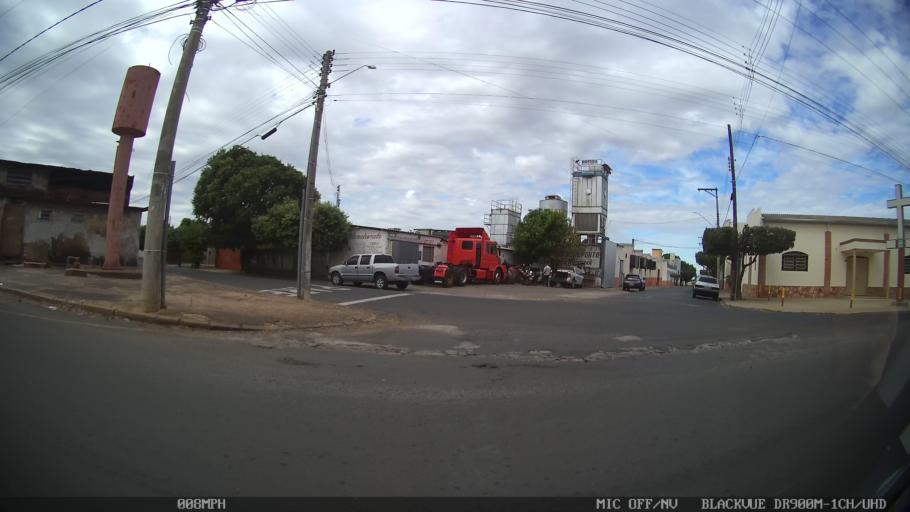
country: BR
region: Sao Paulo
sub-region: Sao Jose Do Rio Preto
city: Sao Jose do Rio Preto
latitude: -20.8124
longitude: -49.4929
